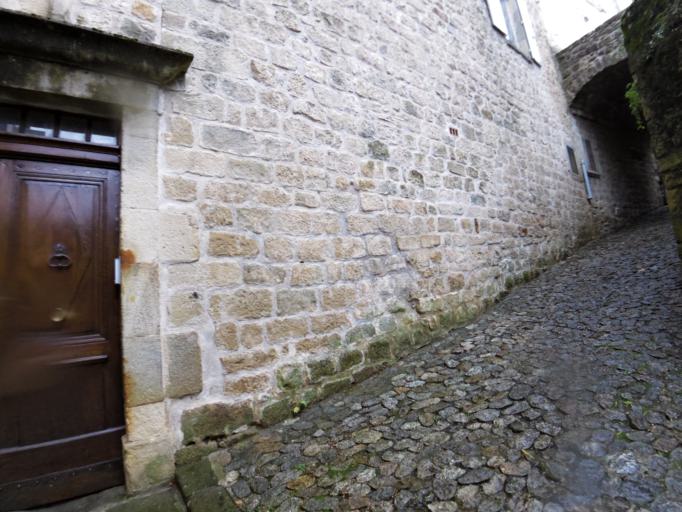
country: FR
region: Rhone-Alpes
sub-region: Departement de l'Ardeche
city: Largentiere
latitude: 44.5416
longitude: 4.2914
